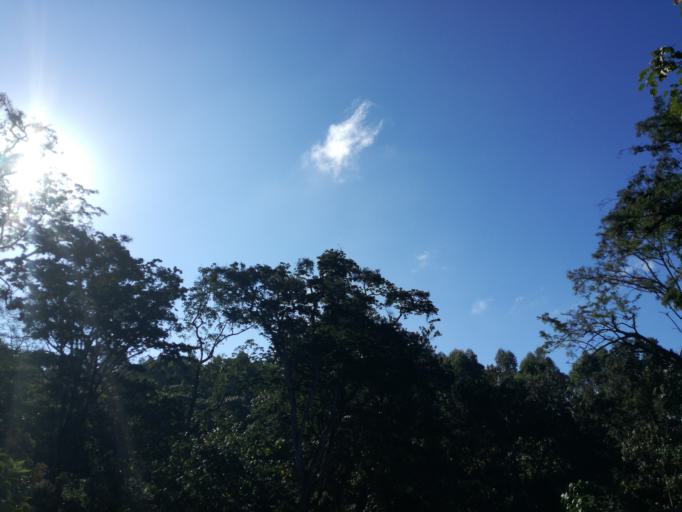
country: KE
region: Kirinyaga
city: Keruguya
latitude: -0.3861
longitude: 37.1398
